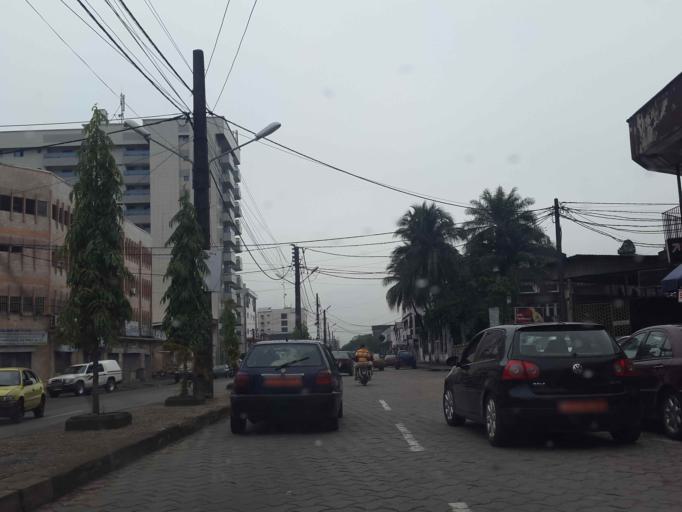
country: CM
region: Littoral
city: Douala
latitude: 4.0478
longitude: 9.7002
